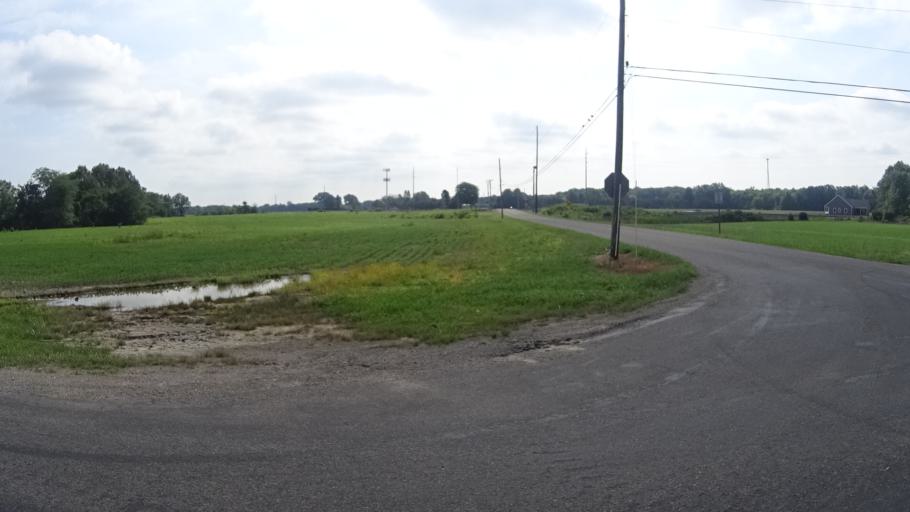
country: US
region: Ohio
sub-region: Lorain County
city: Vermilion
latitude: 41.3829
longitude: -82.4302
